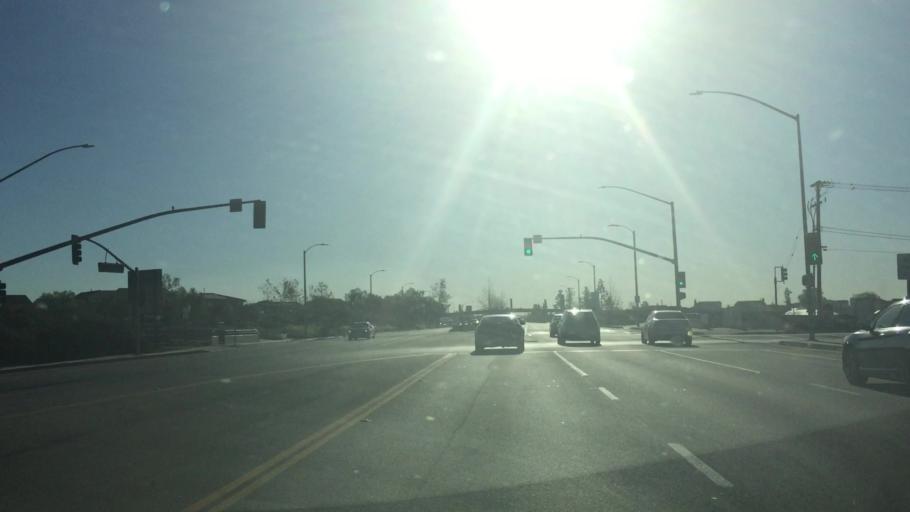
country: US
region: California
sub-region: Orange County
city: Lake Forest
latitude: 33.6961
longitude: -117.7348
